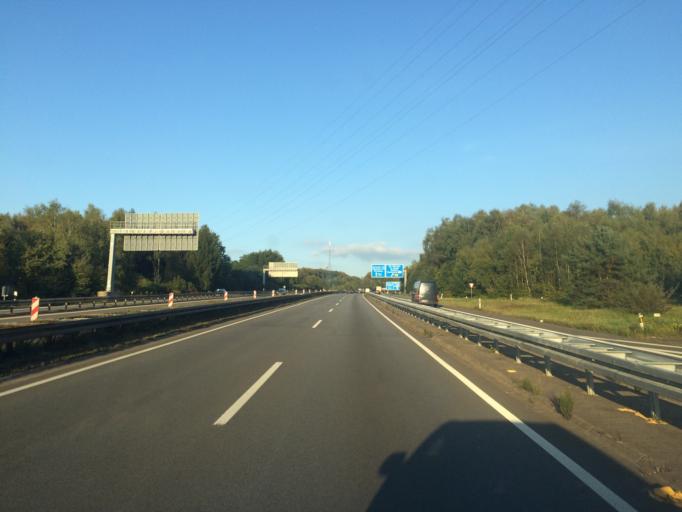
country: DE
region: Saarland
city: Spiesen-Elversberg
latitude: 49.3225
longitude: 7.1518
